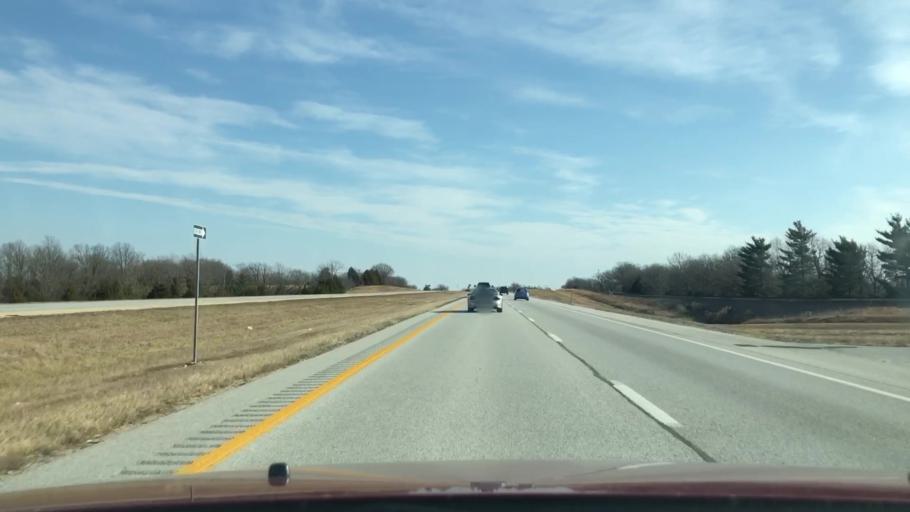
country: US
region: Missouri
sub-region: Webster County
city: Seymour
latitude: 37.1601
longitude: -92.9066
